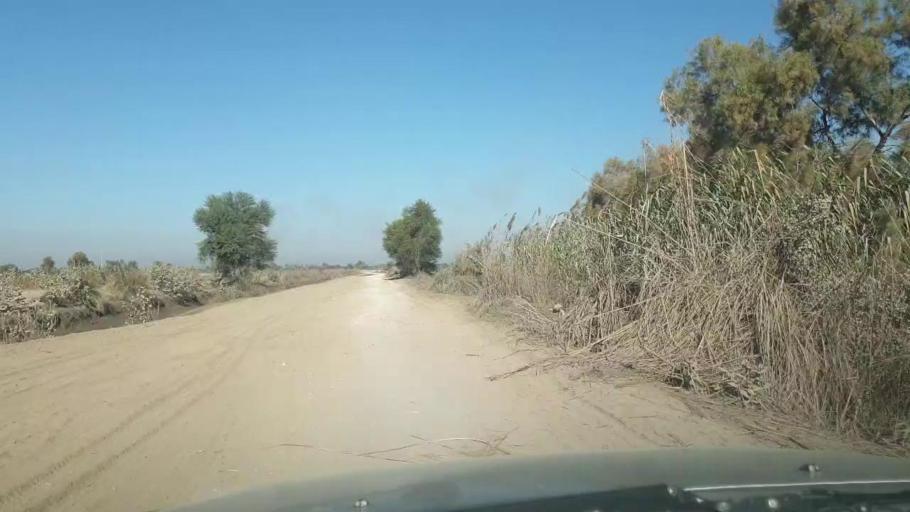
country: PK
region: Sindh
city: Ghotki
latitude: 28.0782
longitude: 69.3459
